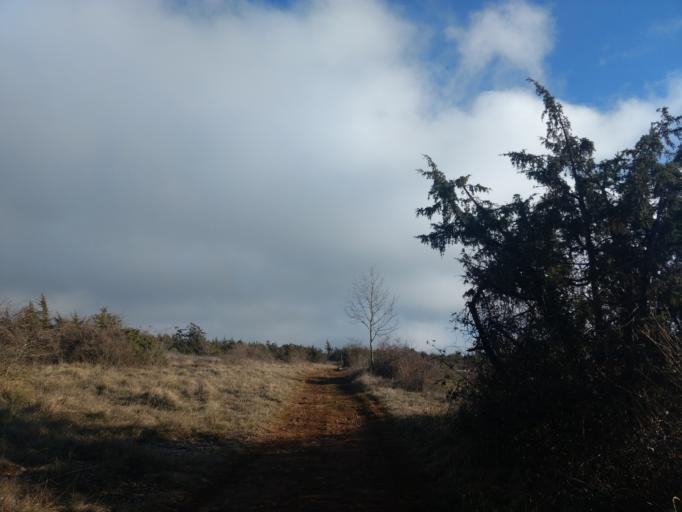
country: FR
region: Midi-Pyrenees
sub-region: Departement de l'Aveyron
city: Salles-la-Source
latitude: 44.4360
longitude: 2.5220
